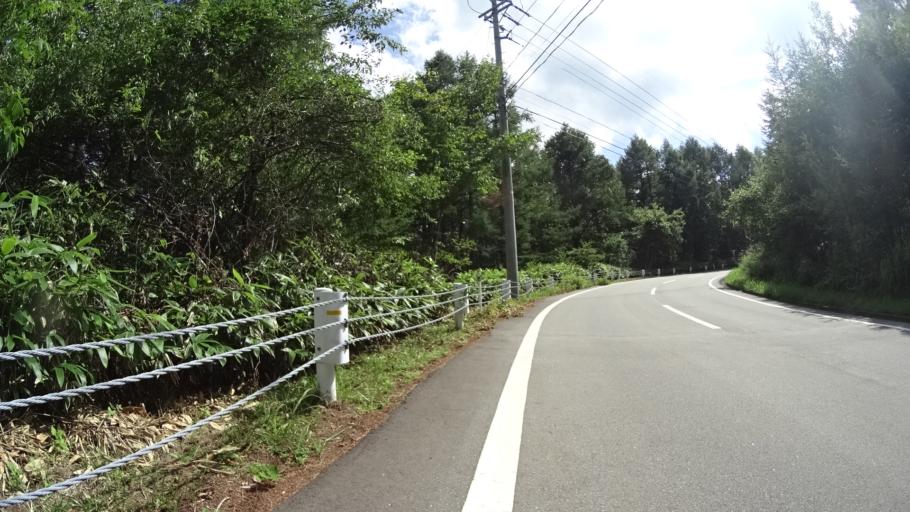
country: JP
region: Nagano
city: Saku
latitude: 36.0496
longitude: 138.4140
